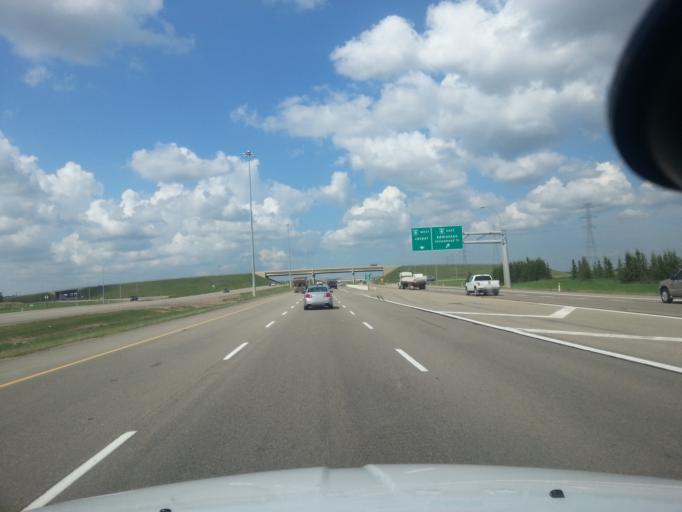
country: CA
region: Alberta
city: St. Albert
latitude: 53.5668
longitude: -113.6607
